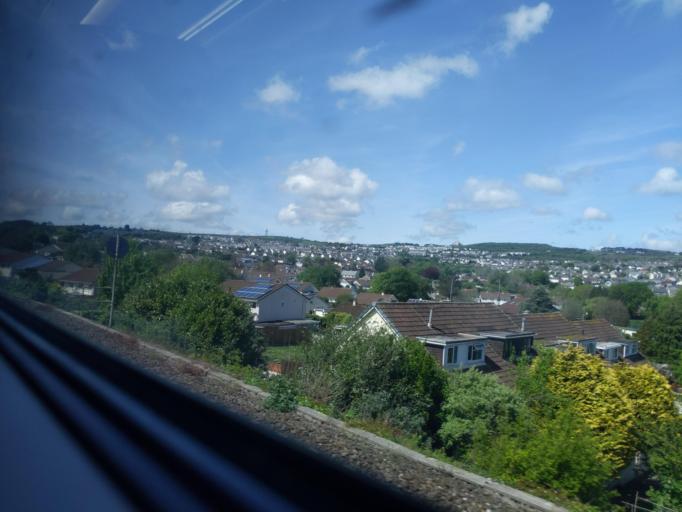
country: GB
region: England
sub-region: Cornwall
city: St Austell
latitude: 50.3389
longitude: -4.7674
